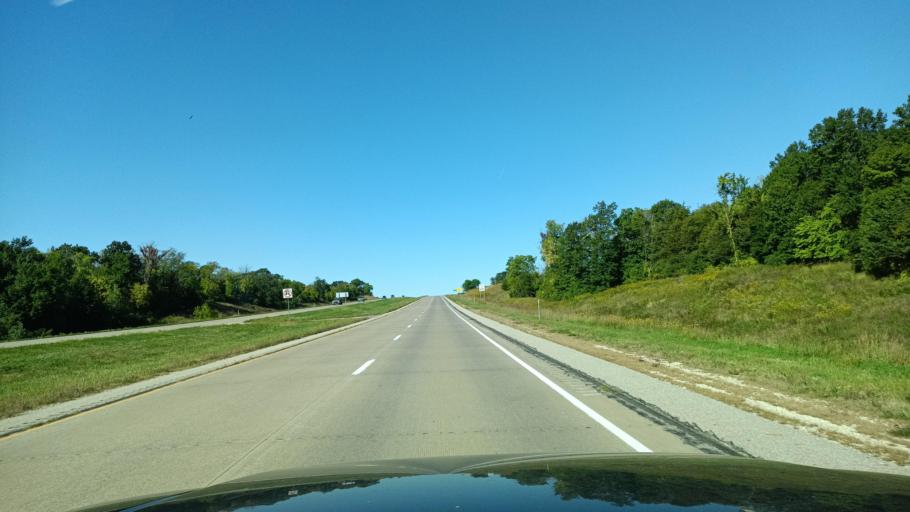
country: US
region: Iowa
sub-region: Lee County
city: Fort Madison
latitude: 40.6708
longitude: -91.2847
